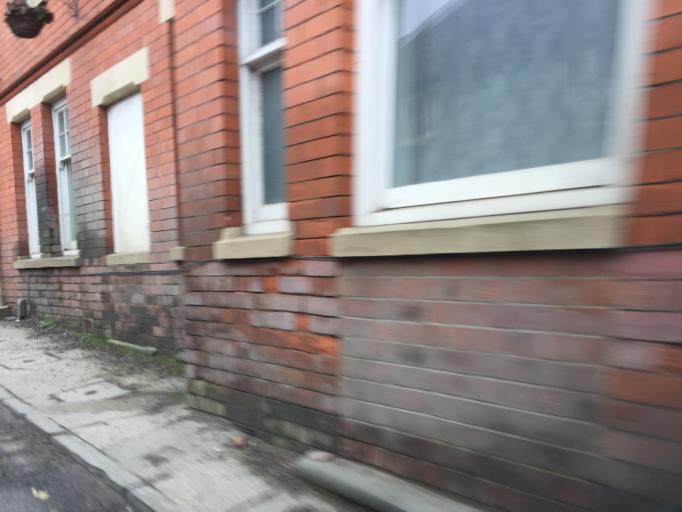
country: GB
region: England
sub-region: Oxfordshire
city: Wantage
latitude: 51.5898
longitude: -1.4285
